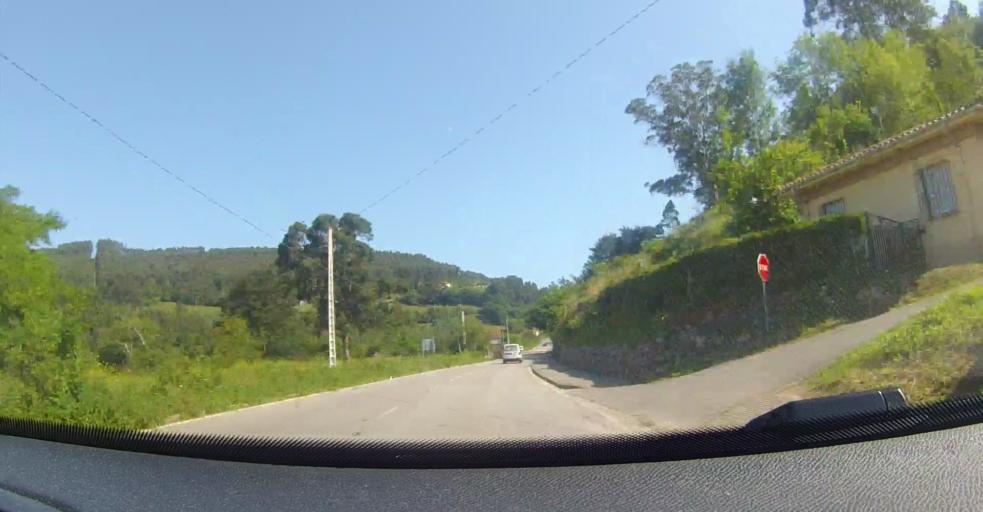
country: ES
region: Asturias
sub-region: Province of Asturias
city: Colunga
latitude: 43.4889
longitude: -5.2694
